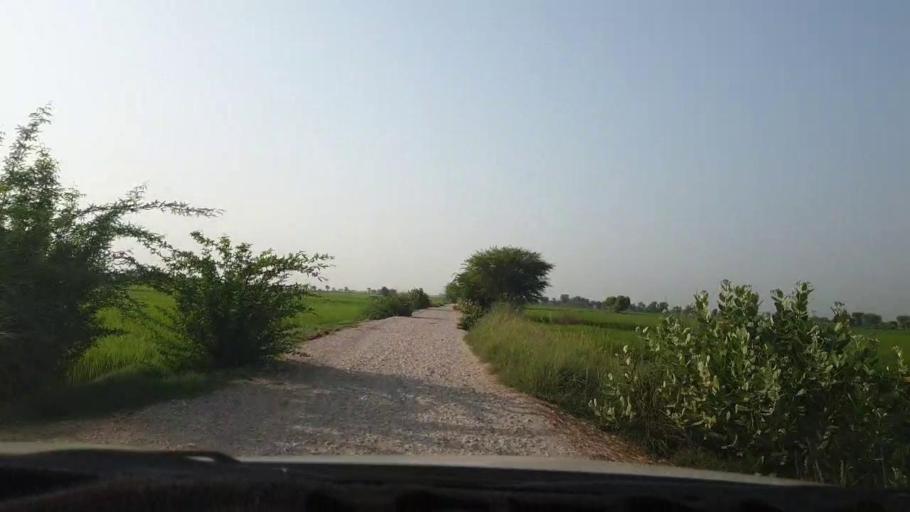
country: PK
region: Sindh
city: Larkana
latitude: 27.5087
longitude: 68.1727
